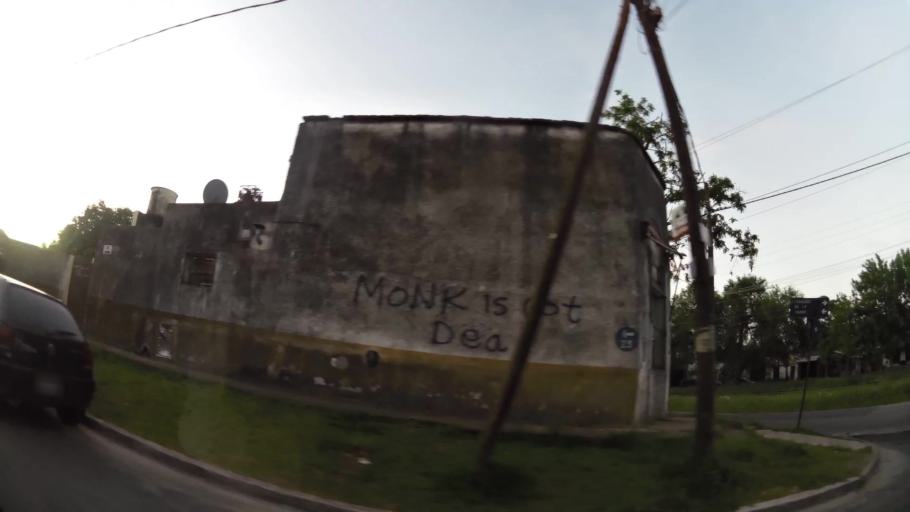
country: AR
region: Buenos Aires
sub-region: Partido de Quilmes
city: Quilmes
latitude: -34.7690
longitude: -58.1990
